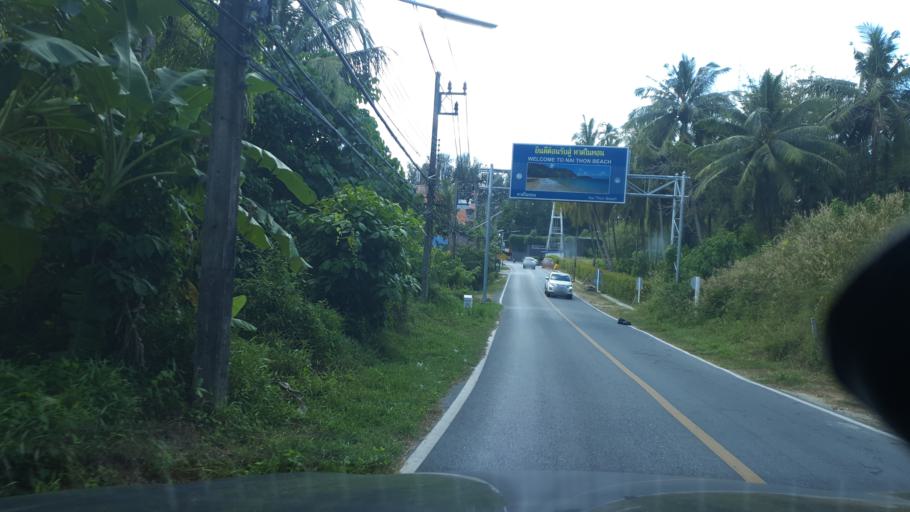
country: TH
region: Phuket
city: Thalang
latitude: 8.0639
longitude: 98.2797
